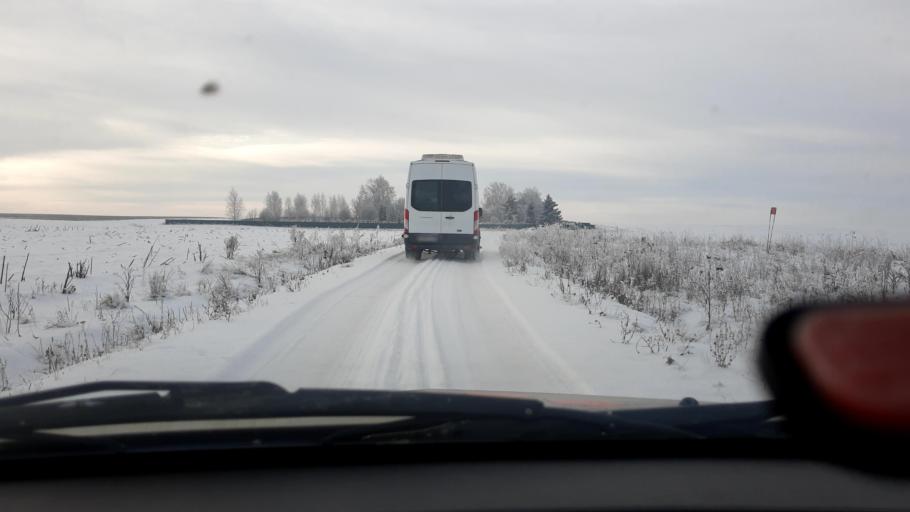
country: RU
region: Bashkortostan
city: Tolbazy
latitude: 54.3543
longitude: 55.8419
